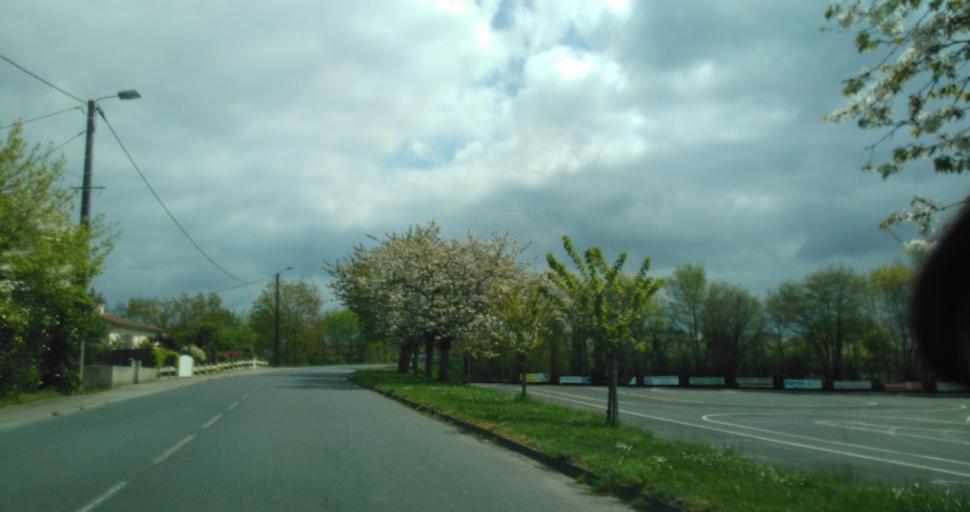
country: FR
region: Poitou-Charentes
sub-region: Departement des Deux-Sevres
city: Moncoutant
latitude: 46.7308
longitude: -0.5949
